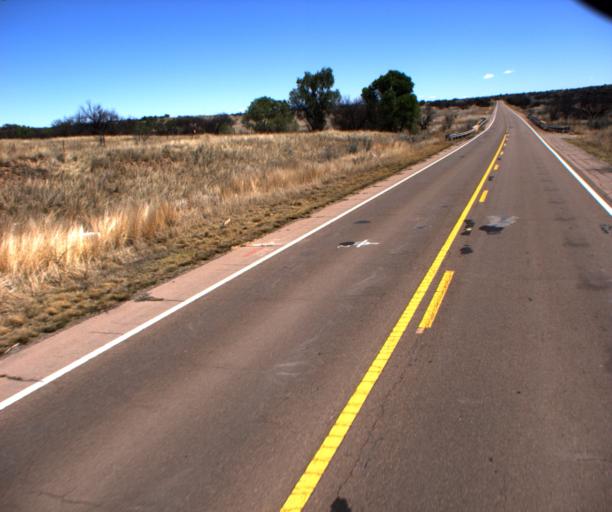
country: US
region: Arizona
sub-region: Pima County
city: Corona de Tucson
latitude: 31.6580
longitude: -110.6991
